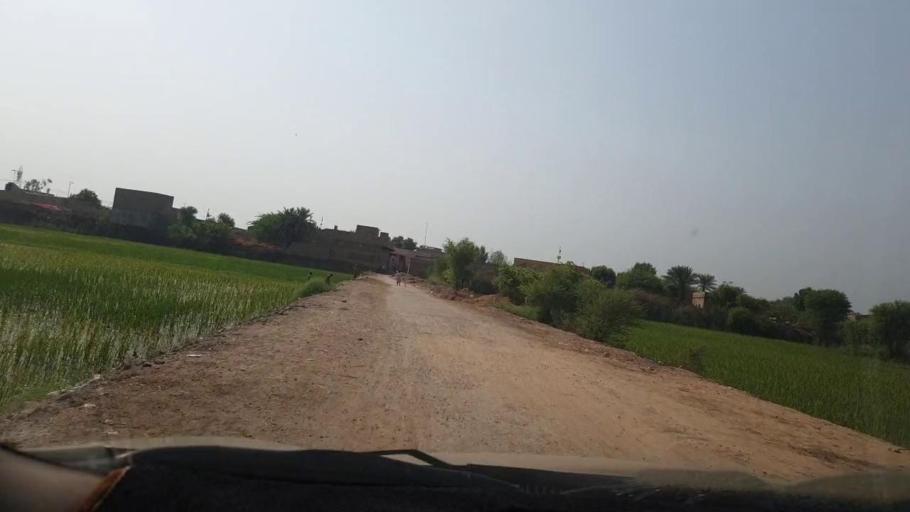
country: PK
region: Sindh
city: Goth Garelo
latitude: 27.4348
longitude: 68.0434
